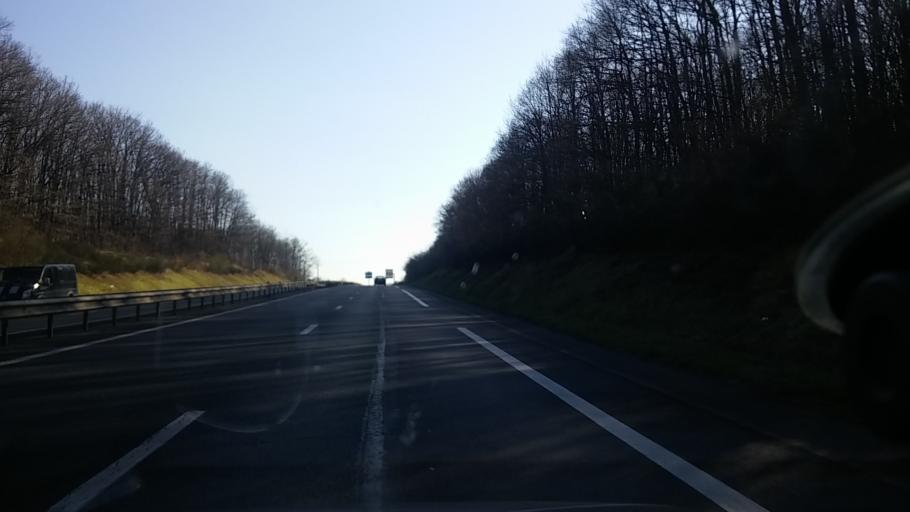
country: FR
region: Centre
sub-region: Departement de l'Indre
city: Saint-Marcel
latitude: 46.6228
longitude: 1.5454
